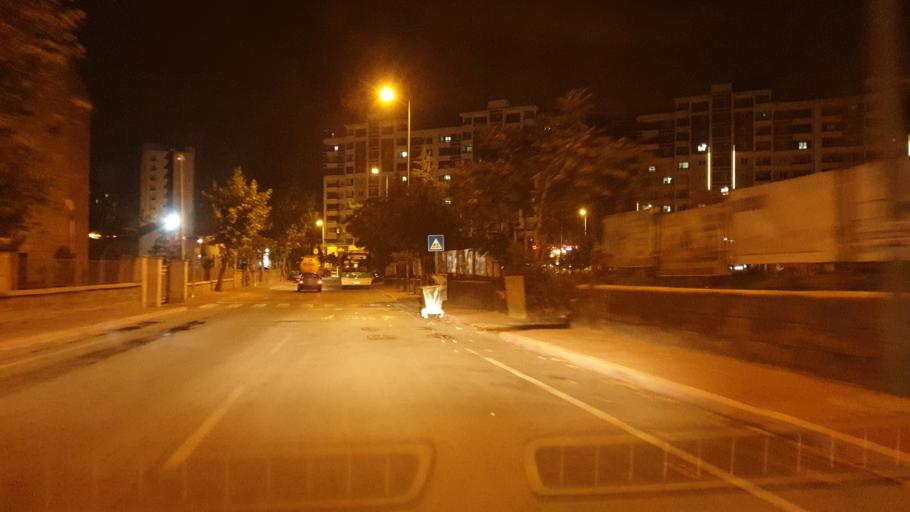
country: TR
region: Kayseri
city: Talas
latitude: 38.6938
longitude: 35.5423
